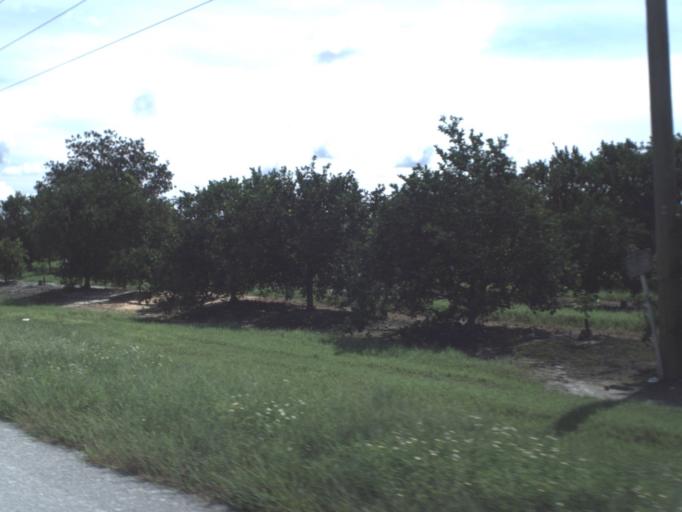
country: US
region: Florida
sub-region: Highlands County
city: Avon Park
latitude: 27.5625
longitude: -81.6485
